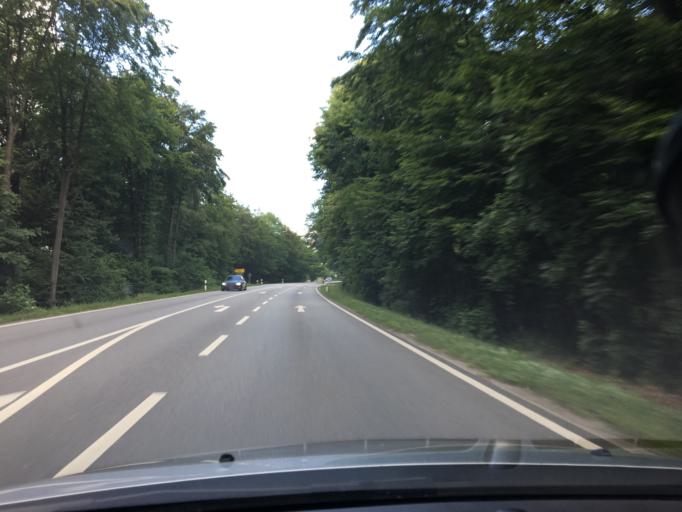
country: DE
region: Bavaria
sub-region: Upper Bavaria
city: Burgkirchen an der Alz
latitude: 48.1773
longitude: 12.7143
